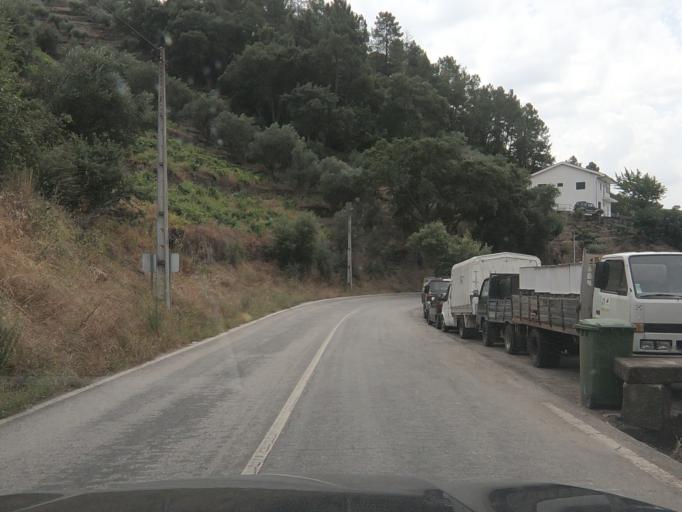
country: PT
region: Vila Real
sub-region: Santa Marta de Penaguiao
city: Santa Marta de Penaguiao
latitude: 41.2373
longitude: -7.7642
